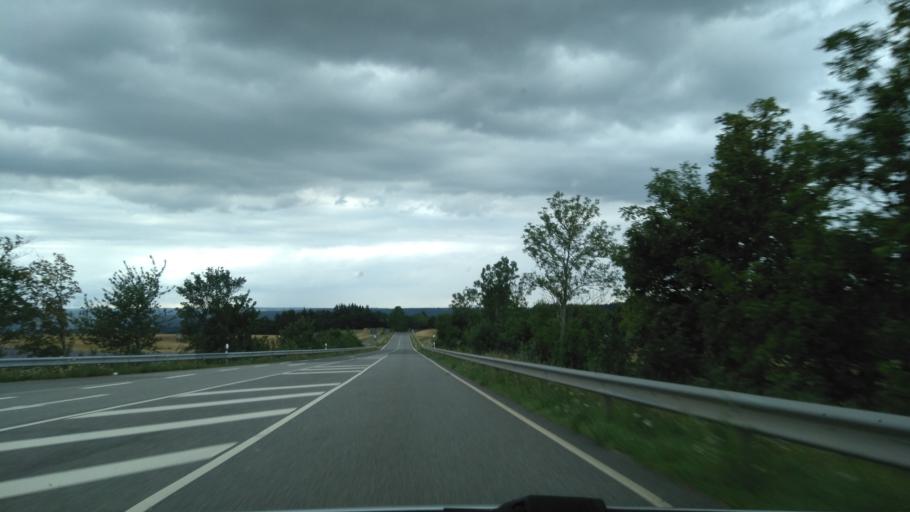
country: DE
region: Rheinland-Pfalz
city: Pellingen
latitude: 49.6851
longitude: 6.6548
